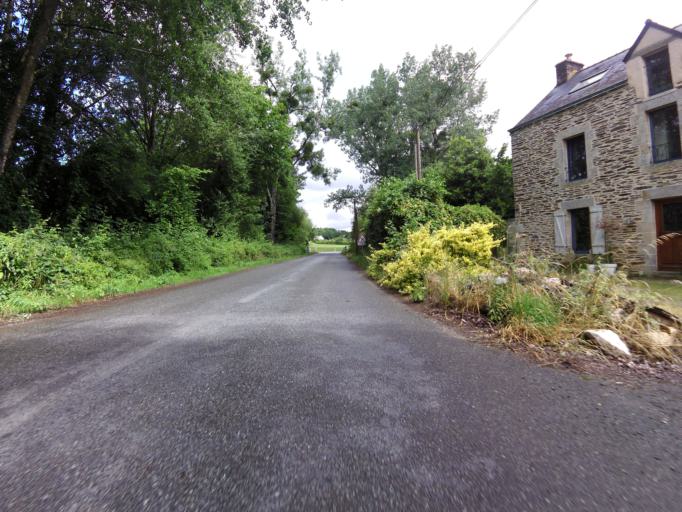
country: FR
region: Brittany
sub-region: Departement du Morbihan
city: Malansac
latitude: 47.7047
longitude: -2.2802
